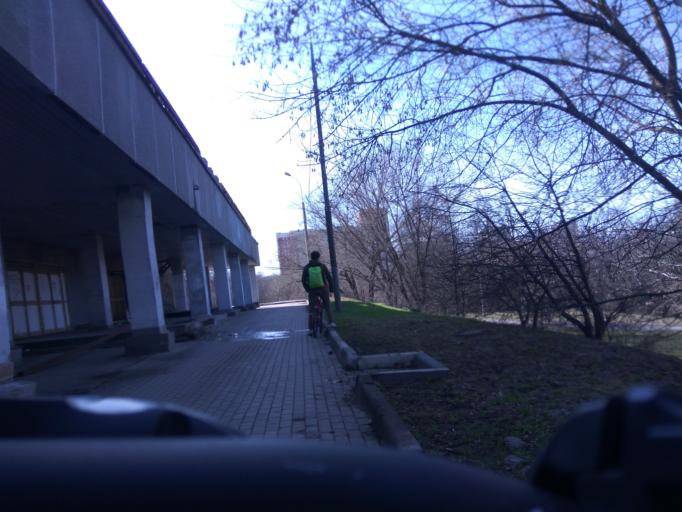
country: RU
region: Moskovskaya
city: Bol'shaya Setun'
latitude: 55.7289
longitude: 37.4410
